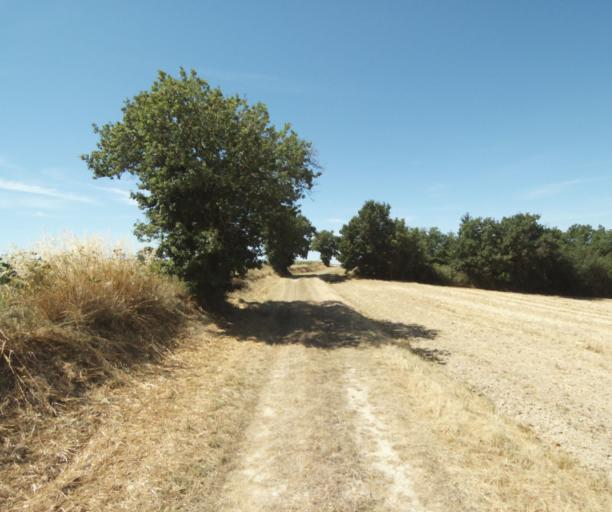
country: FR
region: Midi-Pyrenees
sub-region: Departement de la Haute-Garonne
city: Saint-Felix-Lauragais
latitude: 43.4844
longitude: 1.9200
